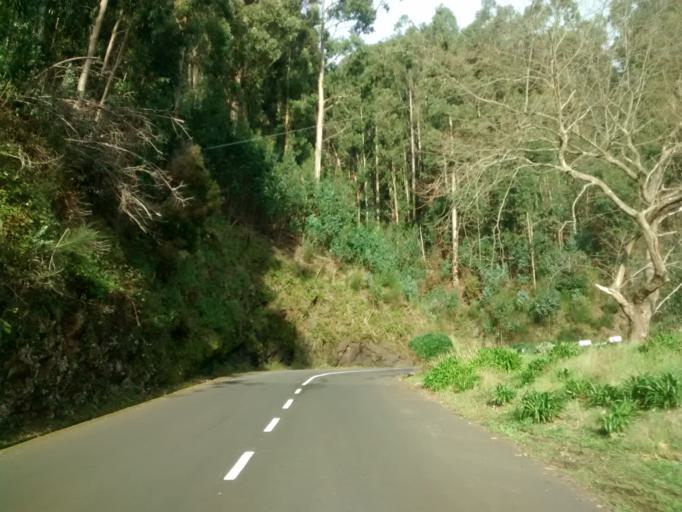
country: PT
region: Madeira
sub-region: Sao Vicente
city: Sao Vicente
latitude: 32.7454
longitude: -17.0254
